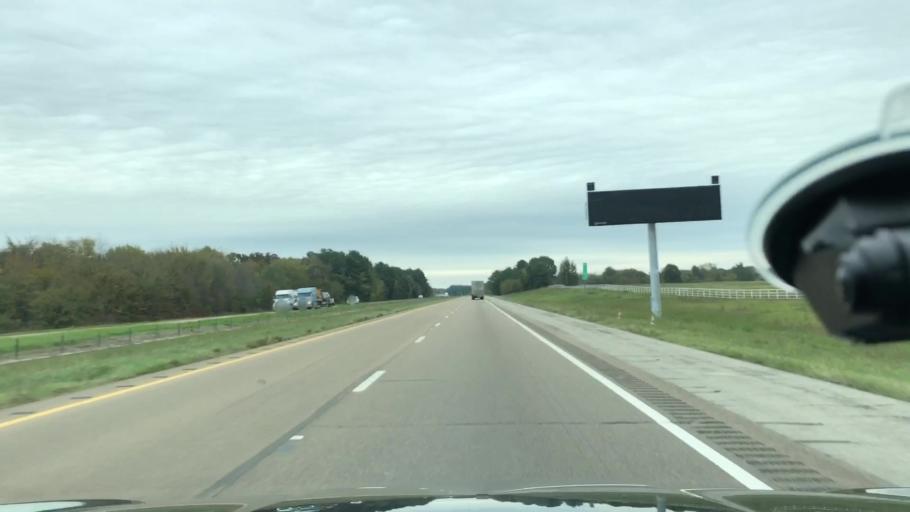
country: US
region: Texas
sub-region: Titus County
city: Mount Pleasant
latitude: 33.2101
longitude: -94.9030
